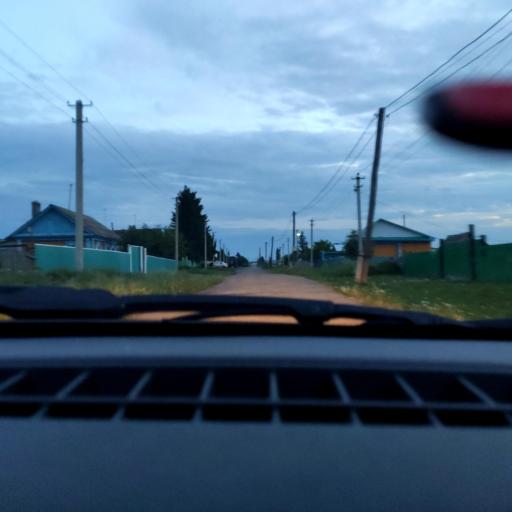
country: RU
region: Bashkortostan
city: Tolbazy
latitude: 54.2906
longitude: 55.8231
